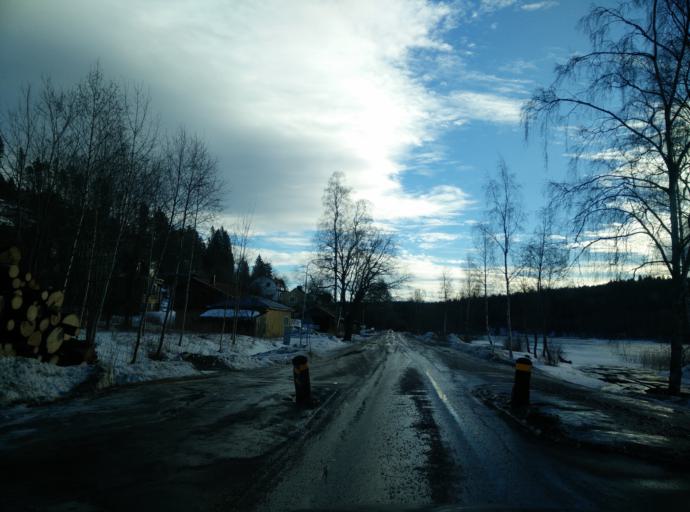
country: SE
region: Vaesternorrland
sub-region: Sundsvalls Kommun
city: Skottsund
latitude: 62.2994
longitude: 17.3944
